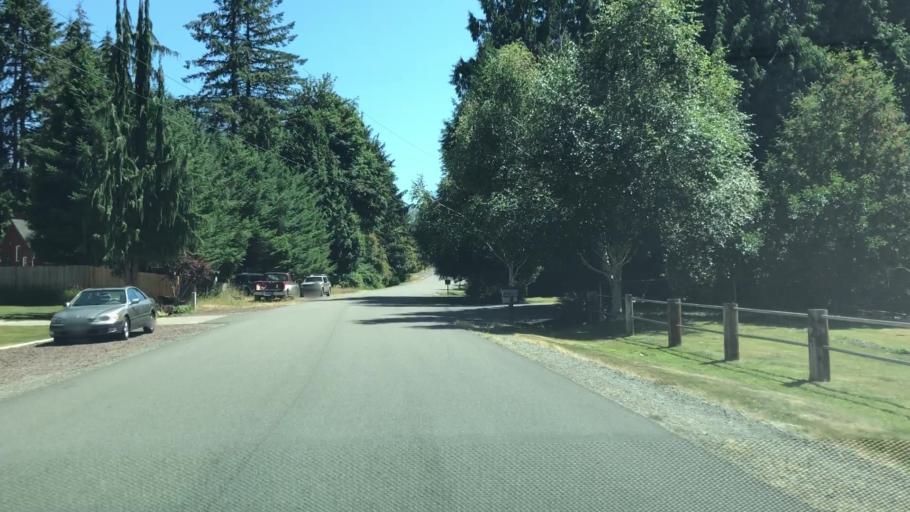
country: US
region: Washington
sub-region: King County
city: Woodinville
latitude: 47.7728
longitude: -122.1345
